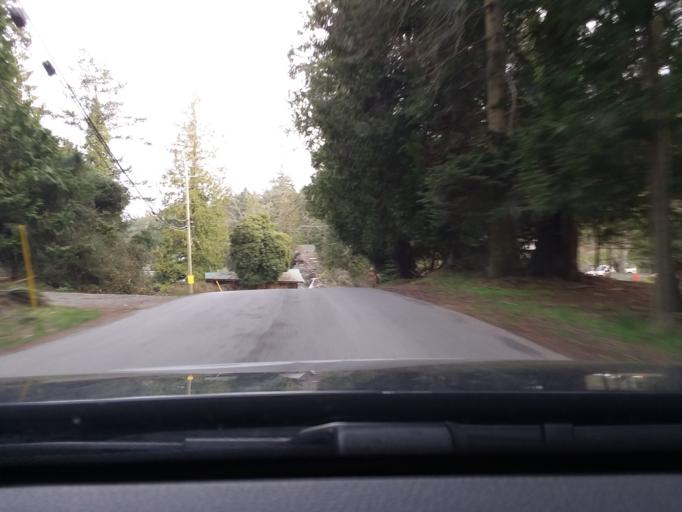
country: CA
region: British Columbia
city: North Saanich
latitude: 48.8787
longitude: -123.3230
